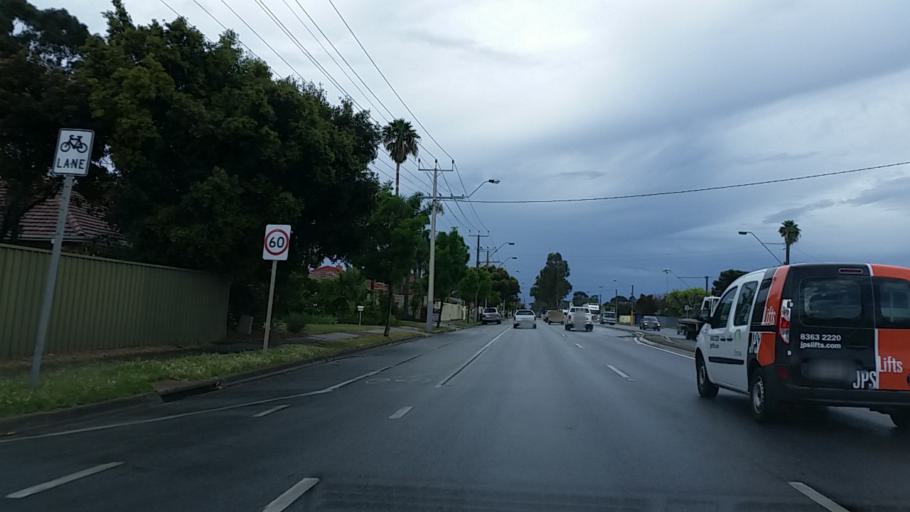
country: AU
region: South Australia
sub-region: Salisbury
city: Salisbury
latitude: -34.7943
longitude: 138.6128
